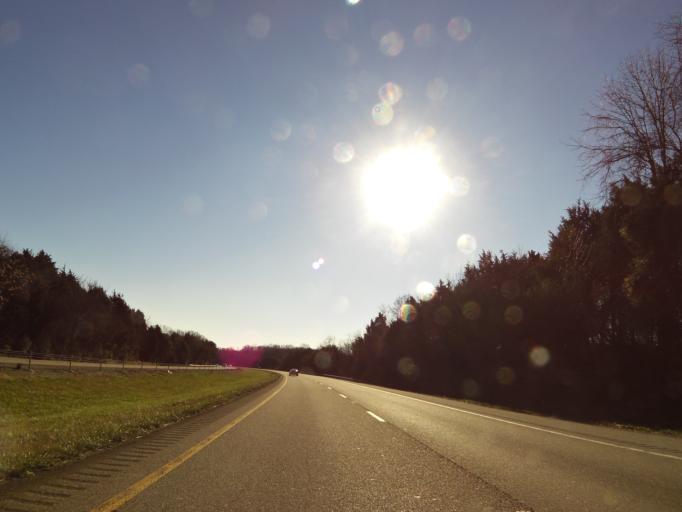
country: US
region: Tennessee
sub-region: Jefferson County
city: Dandridge
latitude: 36.0605
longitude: -83.3762
